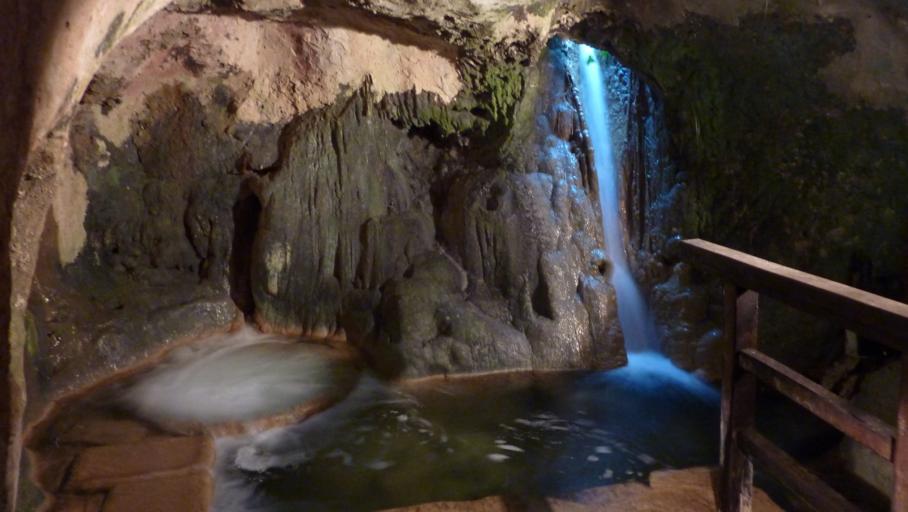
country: HR
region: Sibensko-Kniniska
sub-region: Grad Sibenik
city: Sibenik
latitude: 43.8030
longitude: 15.9647
